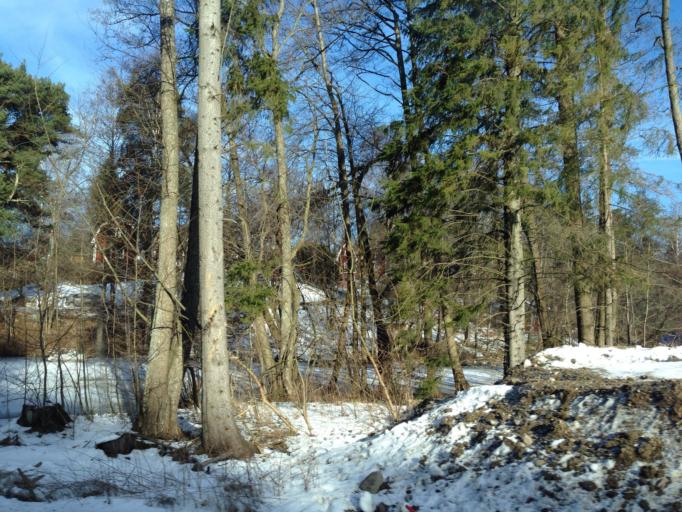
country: SE
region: Stockholm
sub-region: Botkyrka Kommun
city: Fittja
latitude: 59.2755
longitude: 17.8444
